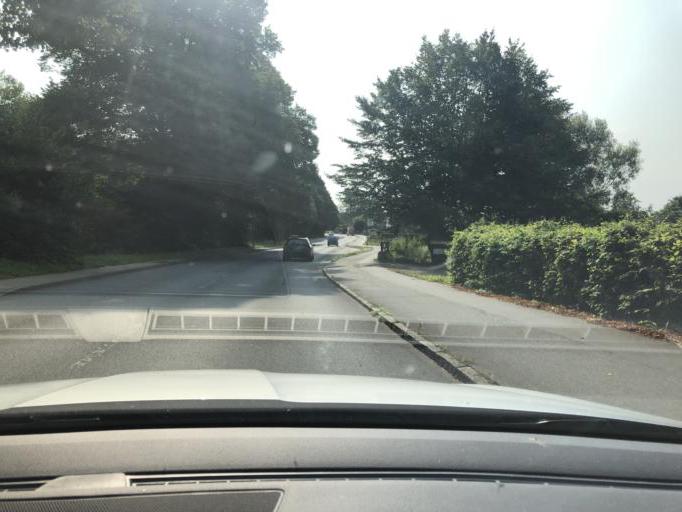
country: DE
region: Schleswig-Holstein
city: Gross Gronau
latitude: 53.8089
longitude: 10.7480
